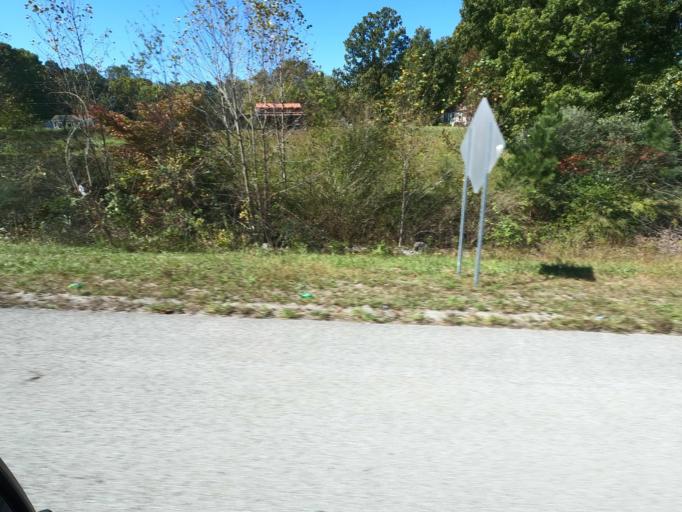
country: US
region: Tennessee
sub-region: Maury County
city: Mount Pleasant
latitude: 35.4507
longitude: -87.2673
